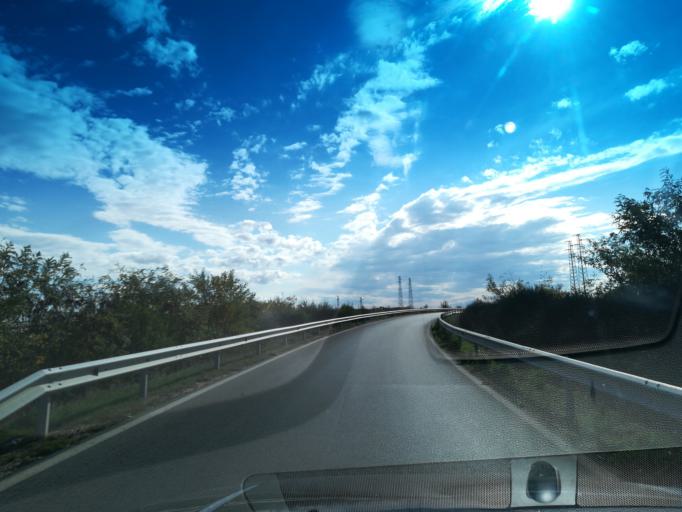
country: BG
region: Stara Zagora
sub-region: Obshtina Stara Zagora
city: Stara Zagora
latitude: 42.3419
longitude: 25.6609
